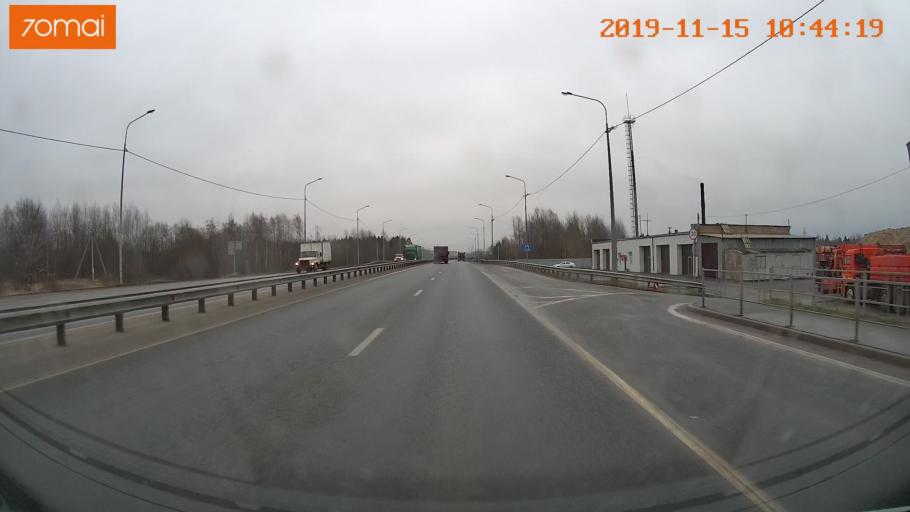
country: RU
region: Vologda
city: Sheksna
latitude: 59.2115
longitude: 38.5549
